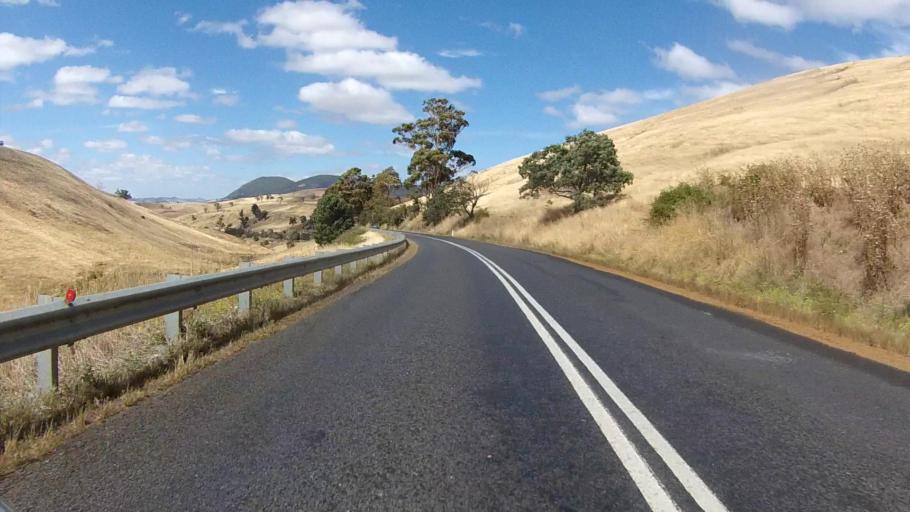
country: AU
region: Tasmania
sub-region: Brighton
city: Bridgewater
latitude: -42.5617
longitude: 147.3912
